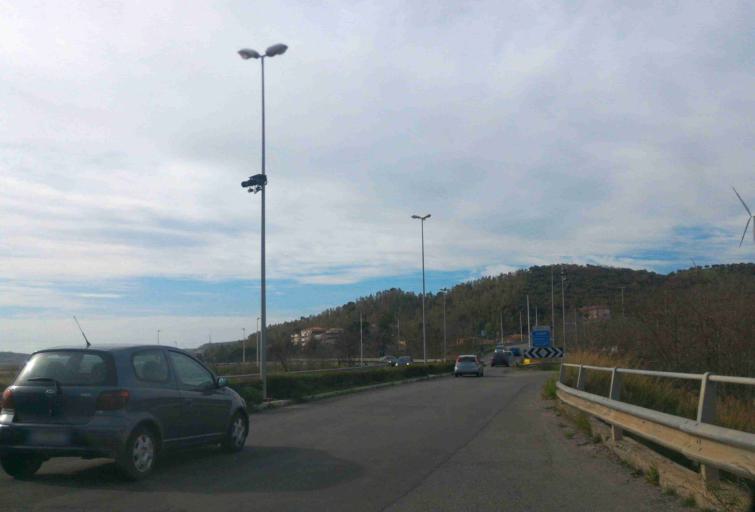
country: IT
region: Calabria
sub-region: Provincia di Crotone
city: Crotone
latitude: 39.0639
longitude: 17.1046
